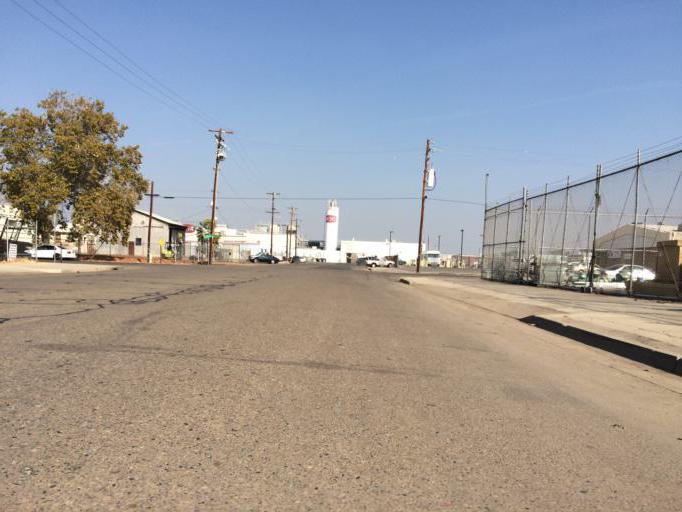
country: US
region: California
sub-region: Fresno County
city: Fresno
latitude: 36.7296
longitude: -119.7788
